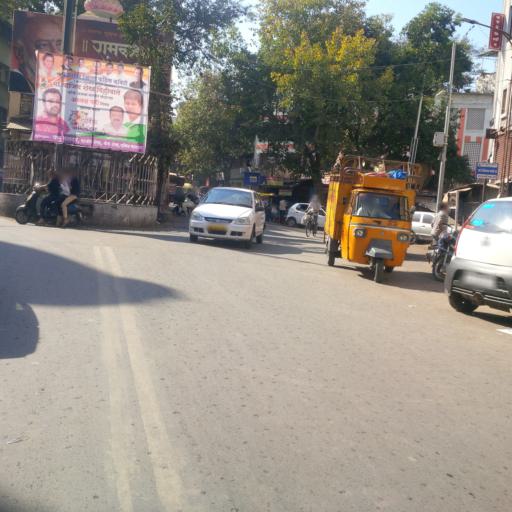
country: IN
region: Maharashtra
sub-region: Pune Division
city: Pune
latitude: 18.5162
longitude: 73.8633
